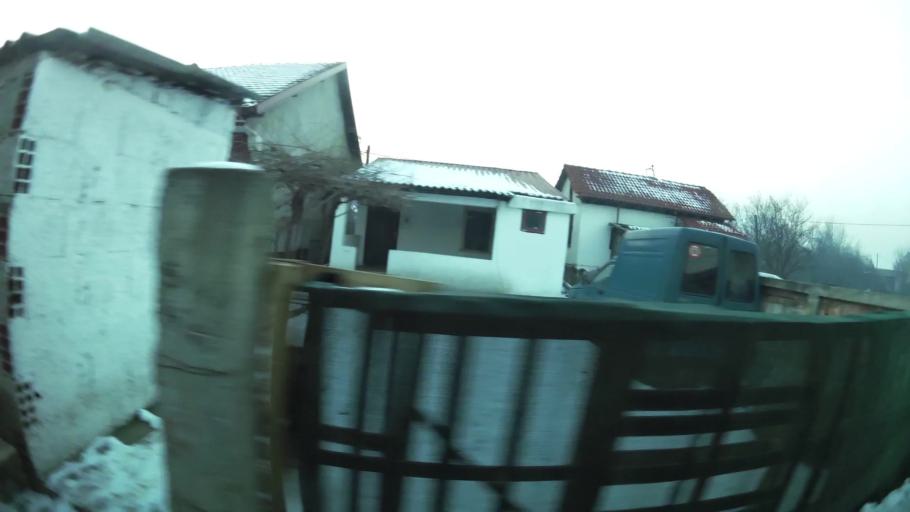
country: MK
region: Kisela Voda
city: Kisela Voda
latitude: 41.9991
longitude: 21.5086
